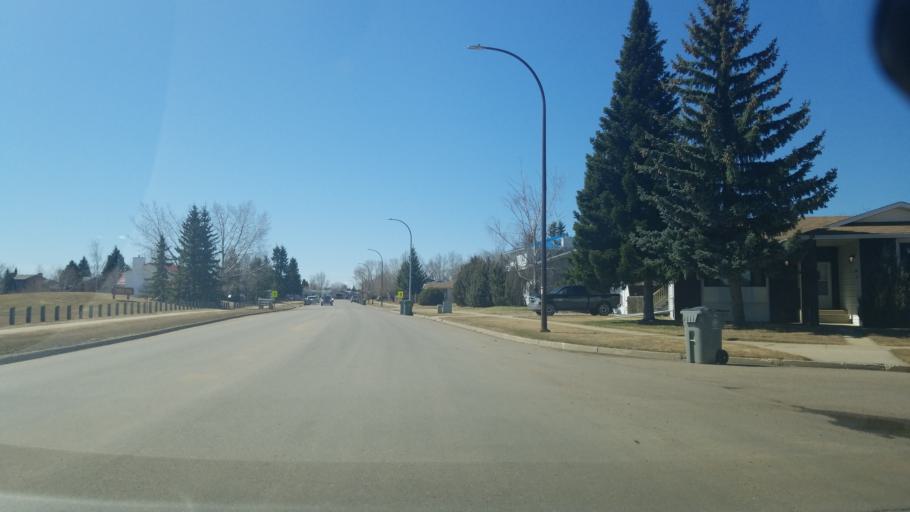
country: CA
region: Saskatchewan
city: Lloydminster
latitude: 53.2629
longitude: -110.0124
